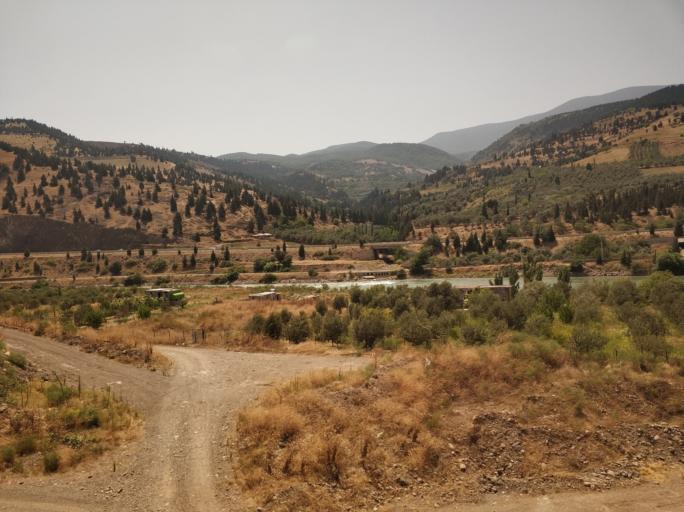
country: IR
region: Gilan
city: Pa'in-e Bazar-e Rudbar
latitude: 36.8495
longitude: 49.4739
